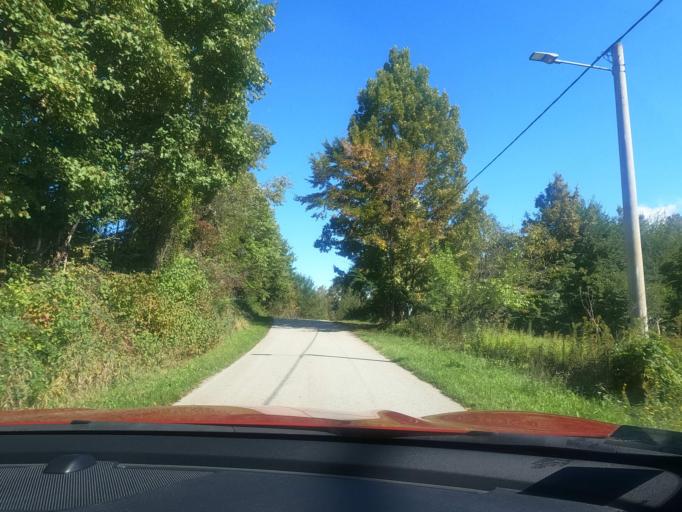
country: HR
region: Sisacko-Moslavacka
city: Petrinja
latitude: 45.3647
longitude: 16.2216
